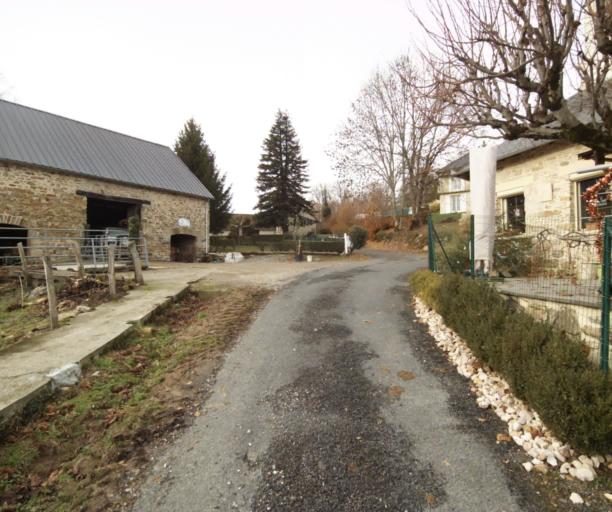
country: FR
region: Limousin
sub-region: Departement de la Correze
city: Saint-Mexant
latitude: 45.2618
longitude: 1.6499
